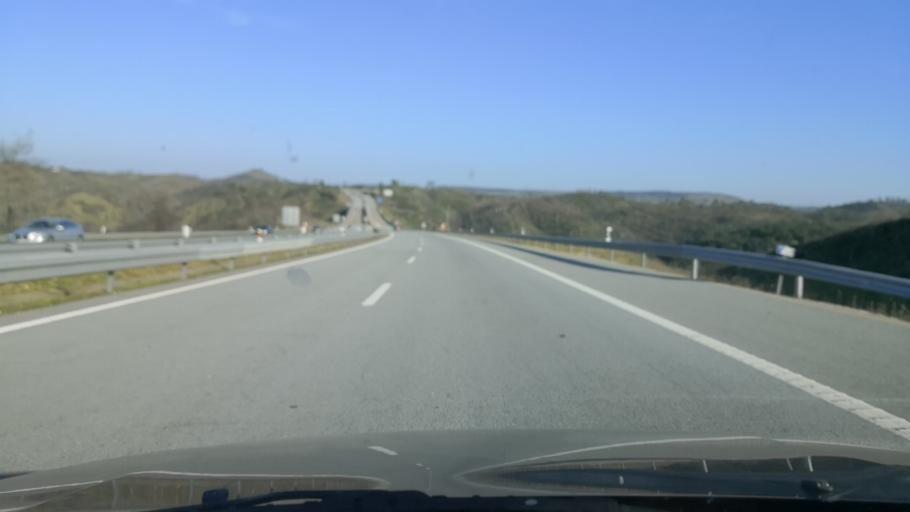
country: PT
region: Portalegre
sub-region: Gaviao
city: Gaviao
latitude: 39.5495
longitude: -7.8320
